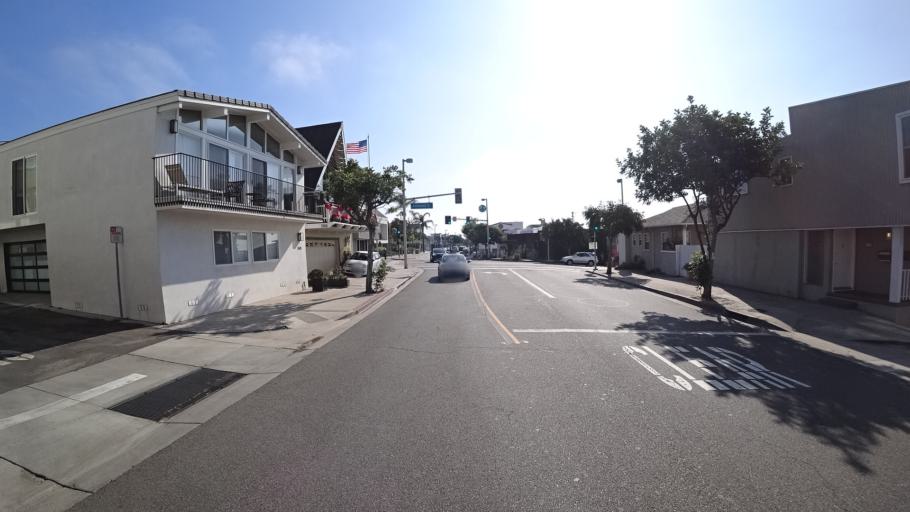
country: US
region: California
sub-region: Los Angeles County
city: Manhattan Beach
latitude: 33.8879
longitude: -118.4114
